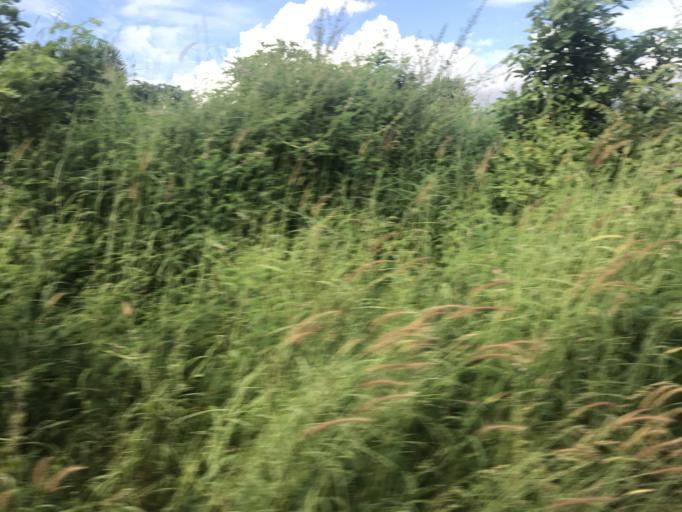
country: IN
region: Kerala
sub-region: Palakkad district
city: Palakkad
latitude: 10.8161
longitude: 76.6852
